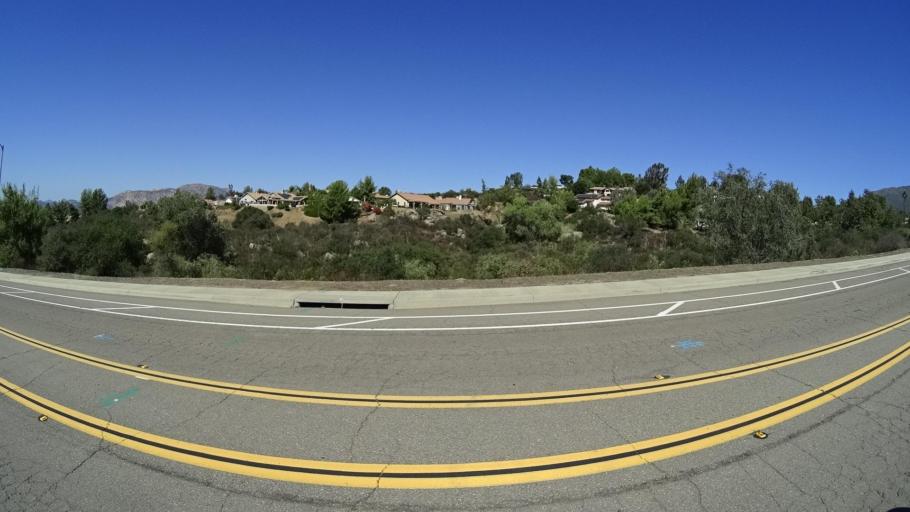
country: US
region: California
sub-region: San Diego County
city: Alpine
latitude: 32.8427
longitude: -116.7728
